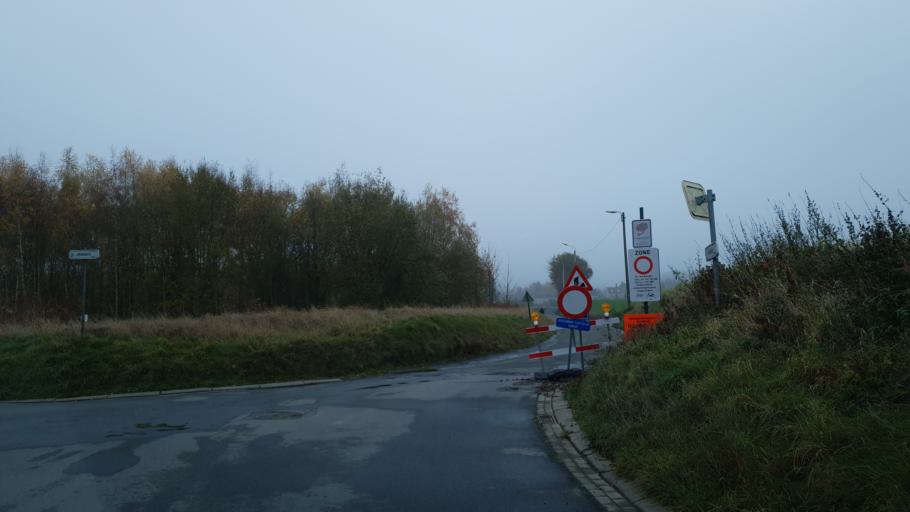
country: BE
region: Flanders
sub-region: Provincie Vlaams-Brabant
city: Kortenberg
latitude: 50.8790
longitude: 4.5304
